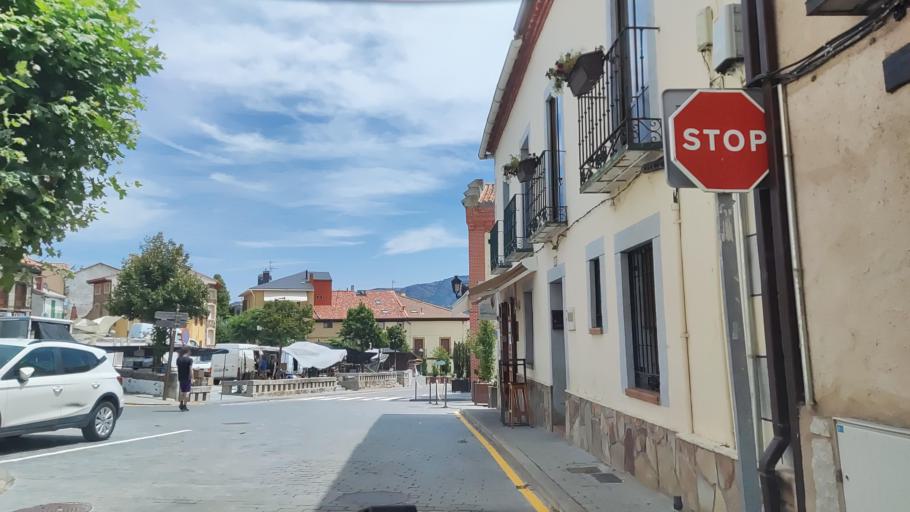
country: ES
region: Madrid
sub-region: Provincia de Madrid
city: Rascafria
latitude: 40.9043
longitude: -3.8808
